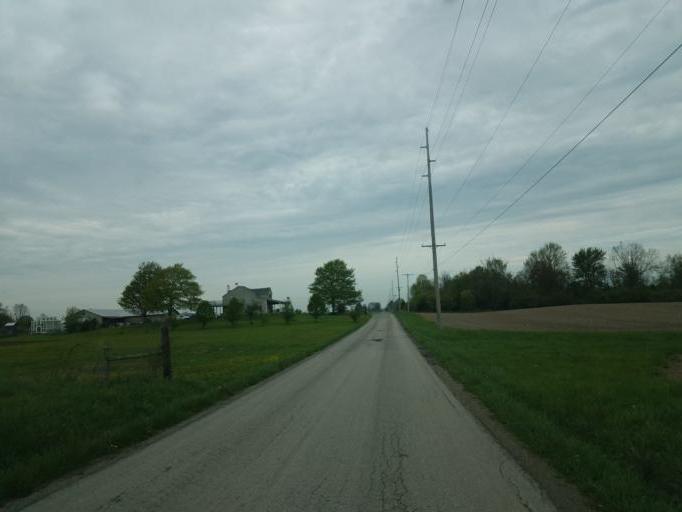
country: US
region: Ohio
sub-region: Richland County
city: Lexington
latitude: 40.6719
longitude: -82.6263
